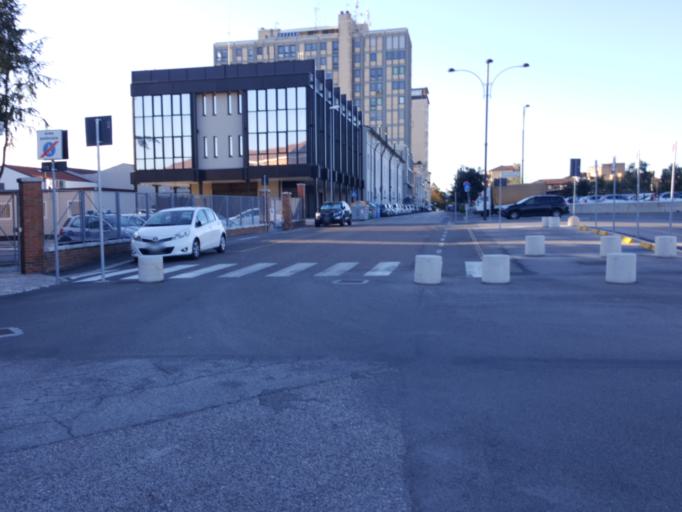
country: IT
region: Emilia-Romagna
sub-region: Provincia di Ravenna
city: Ravenna
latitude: 44.4195
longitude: 12.2095
